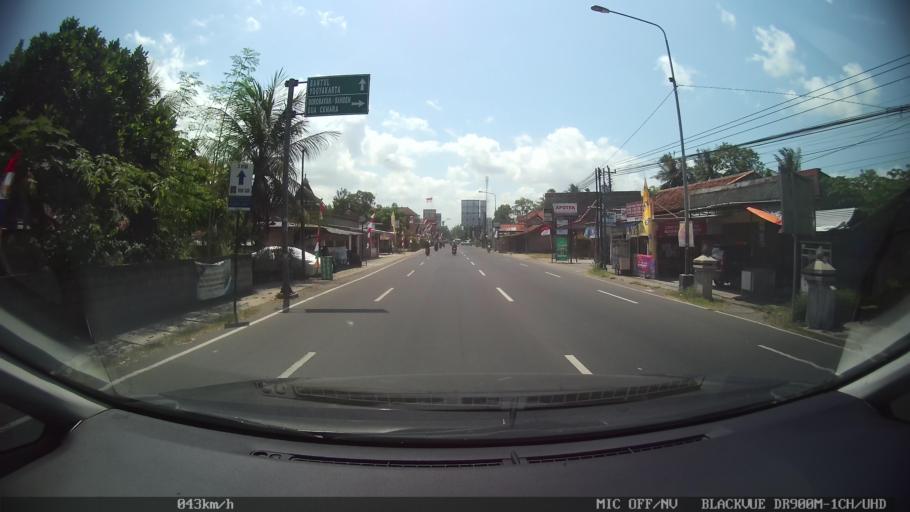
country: ID
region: Daerah Istimewa Yogyakarta
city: Bambanglipuro
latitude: -7.9317
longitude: 110.2717
